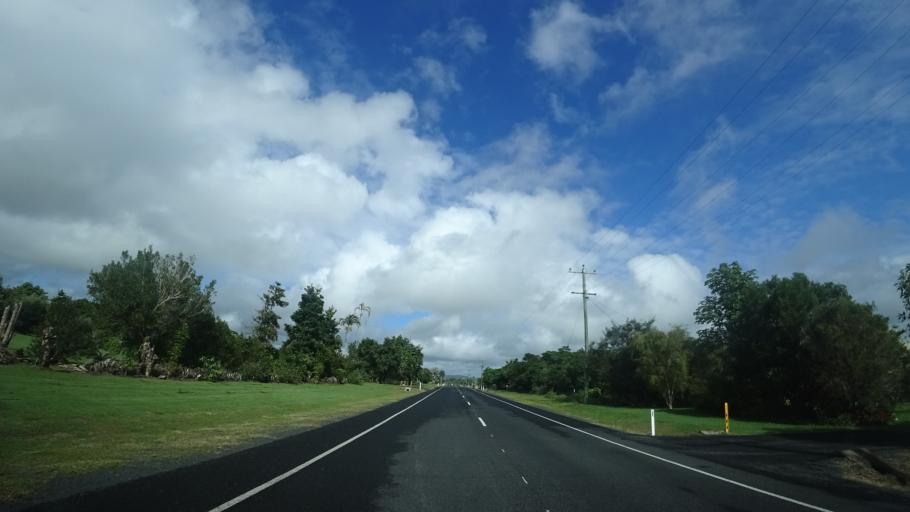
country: AU
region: Queensland
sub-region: Cassowary Coast
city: Innisfail
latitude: -17.5800
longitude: 146.0740
